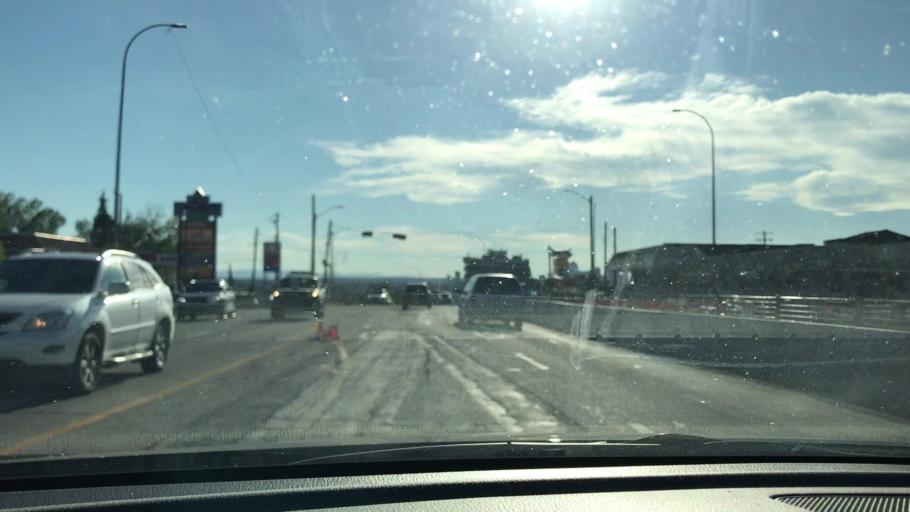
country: CA
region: Alberta
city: Calgary
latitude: 51.0379
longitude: -113.9913
